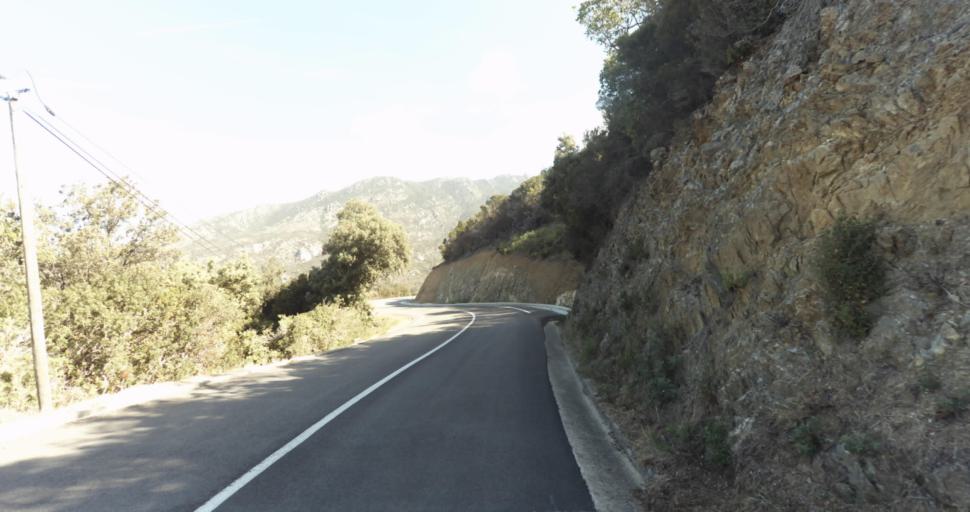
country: FR
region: Corsica
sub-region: Departement de la Corse-du-Sud
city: Ajaccio
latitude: 41.9241
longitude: 8.6428
